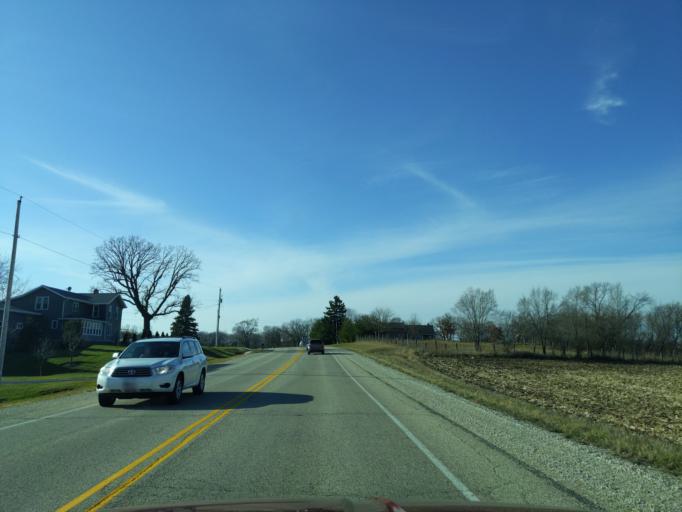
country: US
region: Wisconsin
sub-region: Rock County
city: Milton
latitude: 42.8244
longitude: -88.9071
